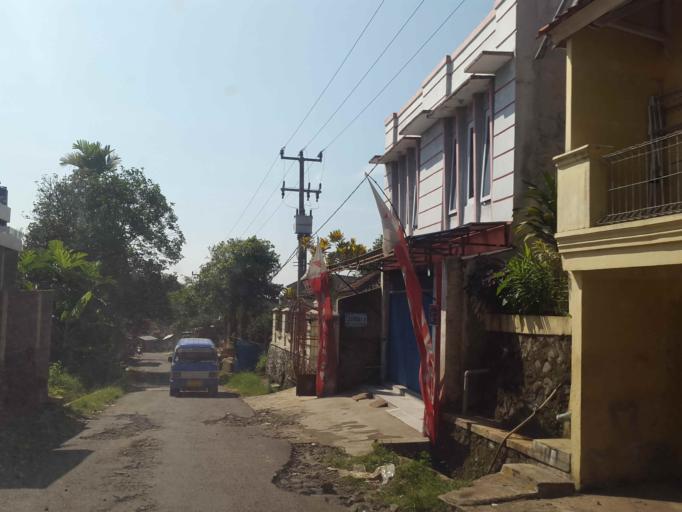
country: ID
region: West Java
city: Sukabumi
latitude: -6.8329
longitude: 107.0643
